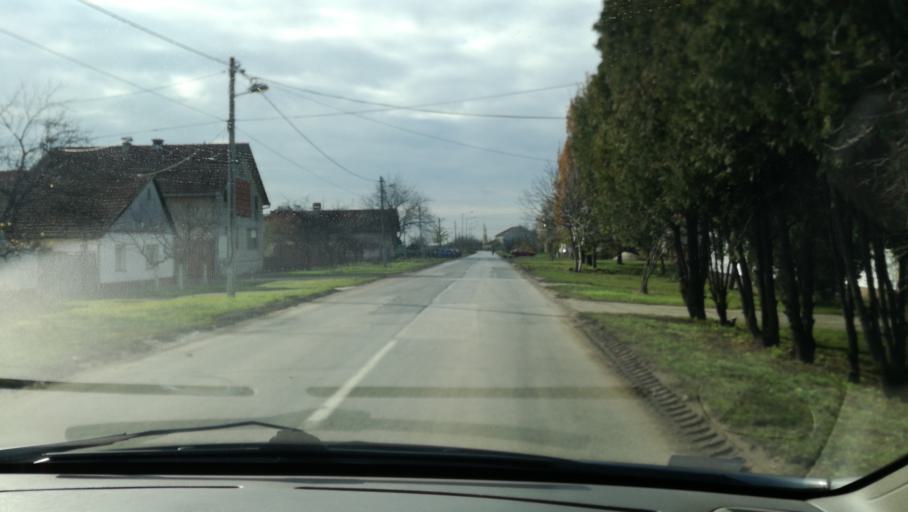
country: RS
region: Autonomna Pokrajina Vojvodina
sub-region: Severnobanatski Okrug
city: Kikinda
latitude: 45.8268
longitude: 20.4335
